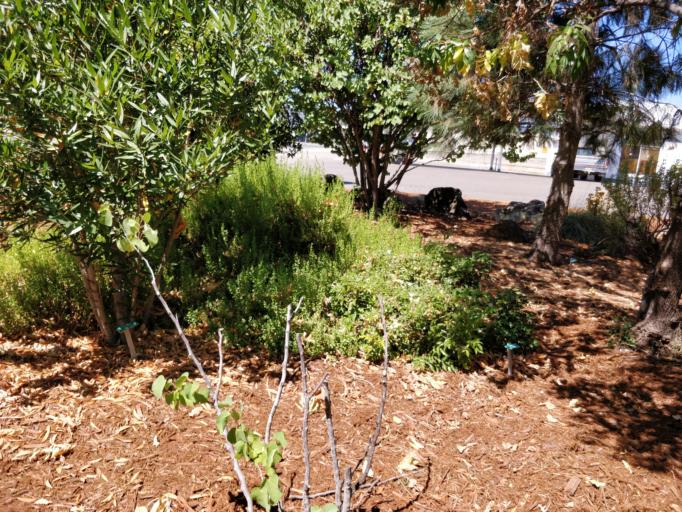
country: US
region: California
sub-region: Shasta County
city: Shasta Lake
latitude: 40.6808
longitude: -122.3678
